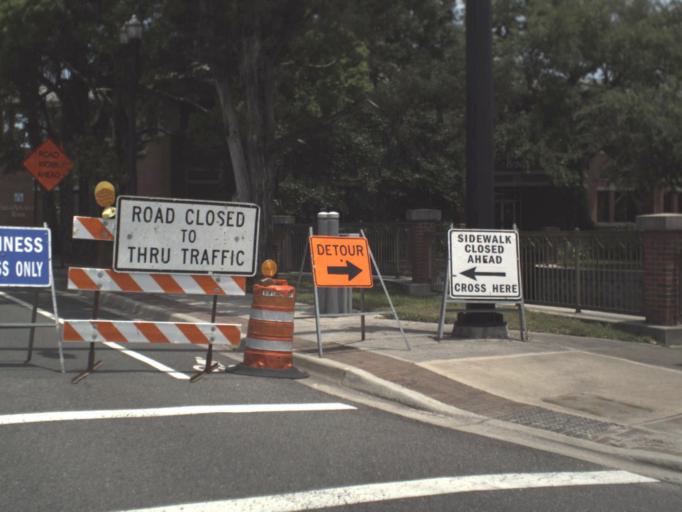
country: US
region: Florida
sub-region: Duval County
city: Jacksonville
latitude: 30.3122
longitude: -81.6547
